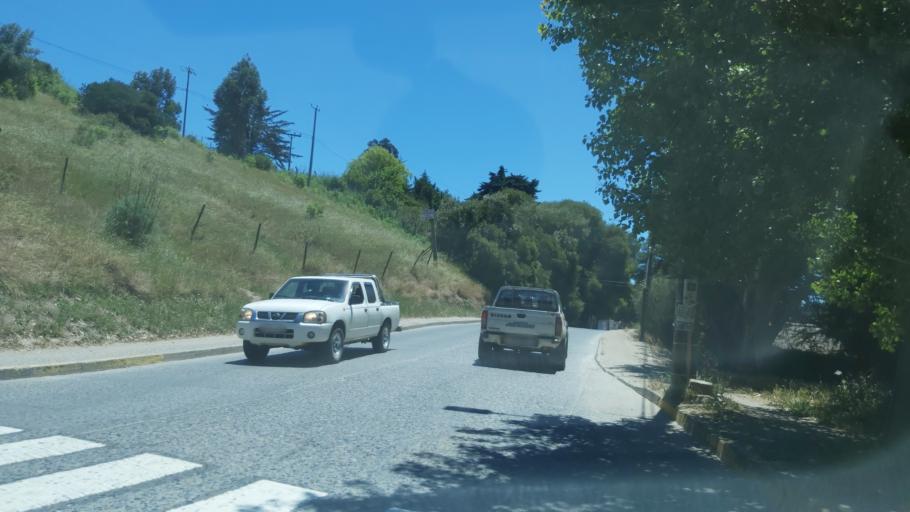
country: CL
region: Maule
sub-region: Provincia de Talca
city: Constitucion
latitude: -35.3421
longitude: -72.3966
